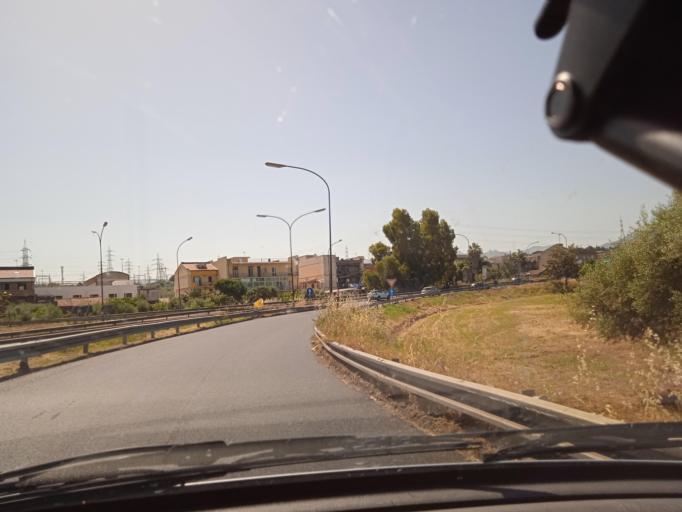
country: IT
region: Sicily
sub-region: Messina
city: San Filippo del Mela
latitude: 38.1912
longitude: 15.2739
